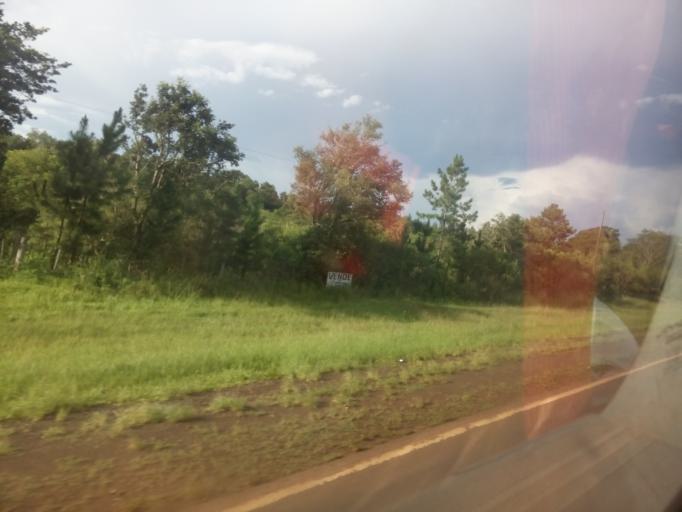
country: AR
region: Misiones
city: Santa Ana
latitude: -27.3862
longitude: -55.5911
